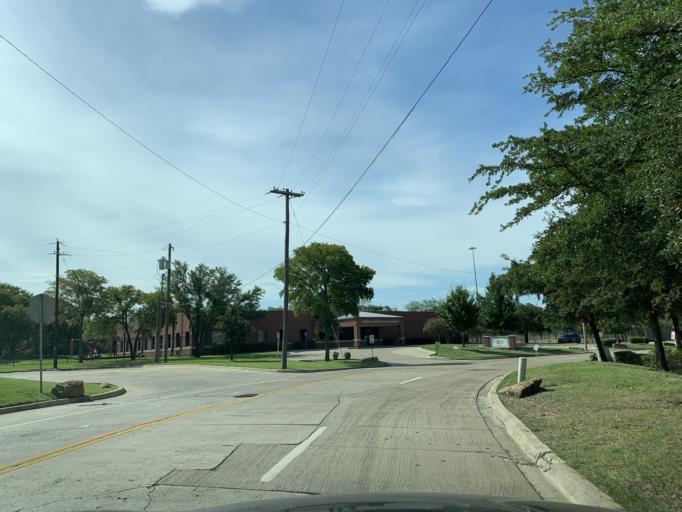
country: US
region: Texas
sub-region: Dallas County
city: Cockrell Hill
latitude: 32.7701
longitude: -96.8806
